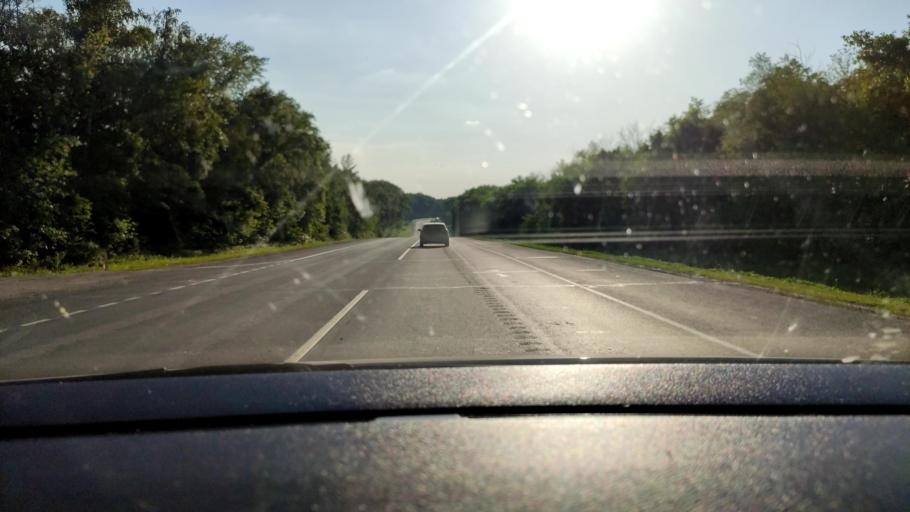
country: RU
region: Voronezj
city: Kashirskoye
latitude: 51.4905
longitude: 39.6194
